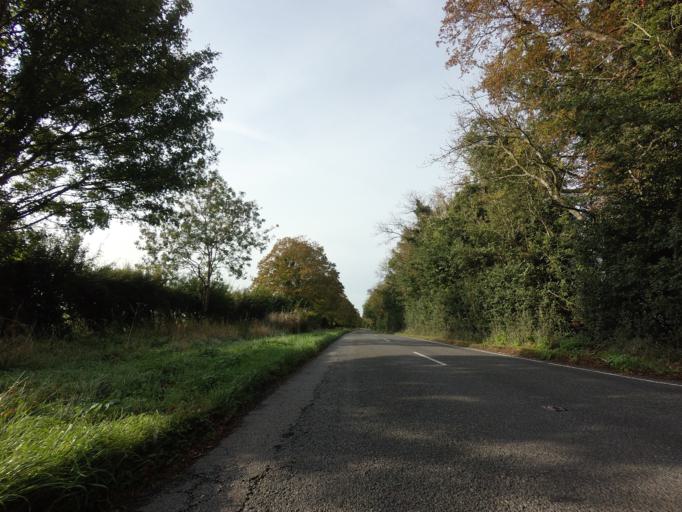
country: GB
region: England
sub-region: Cambridgeshire
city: Harston
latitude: 52.1133
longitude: 0.0941
